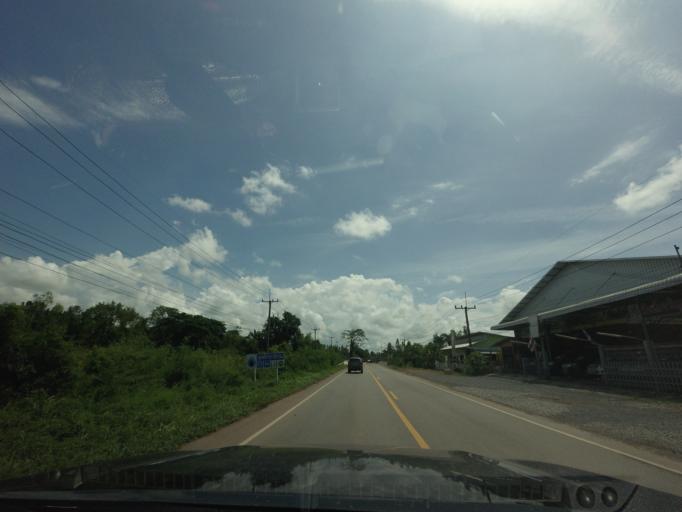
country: TH
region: Changwat Udon Thani
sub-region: Amphoe Ban Phue
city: Ban Phue
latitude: 17.6993
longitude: 102.4458
